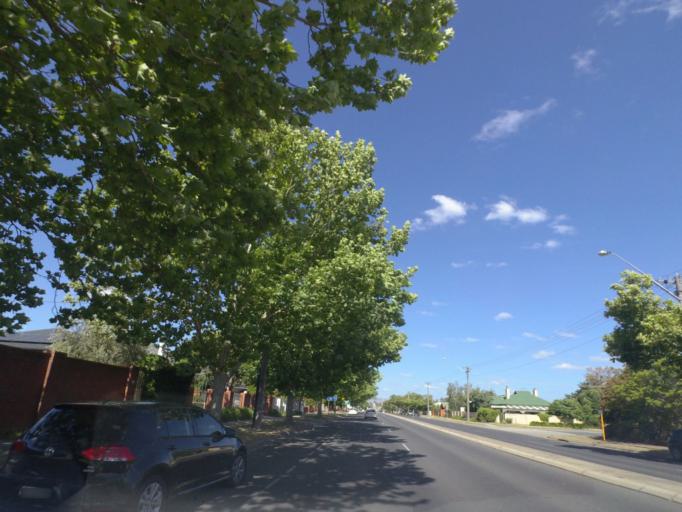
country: AU
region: New South Wales
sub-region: Albury Municipality
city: Albury
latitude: -36.0683
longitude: 146.9279
